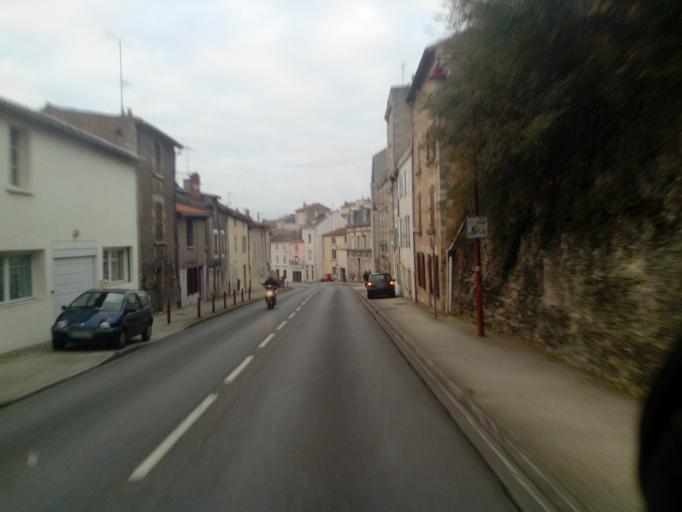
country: FR
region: Poitou-Charentes
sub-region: Departement de la Vienne
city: Poitiers
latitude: 46.5747
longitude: 0.3550
